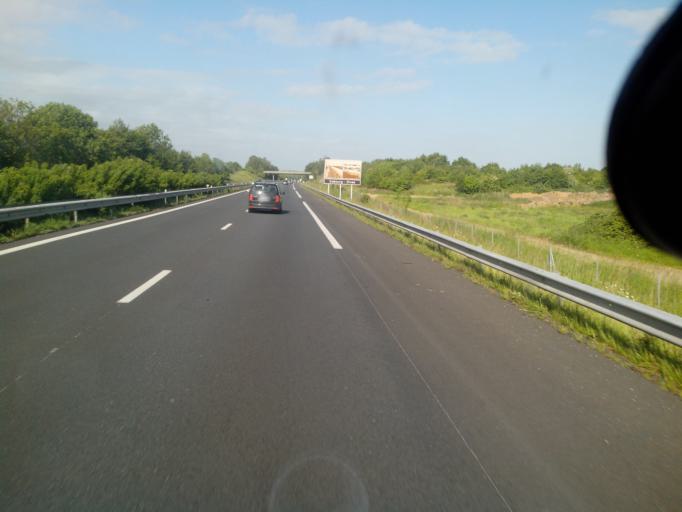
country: FR
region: Lower Normandy
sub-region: Departement du Calvados
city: Dives-sur-Mer
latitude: 49.2204
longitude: -0.1146
